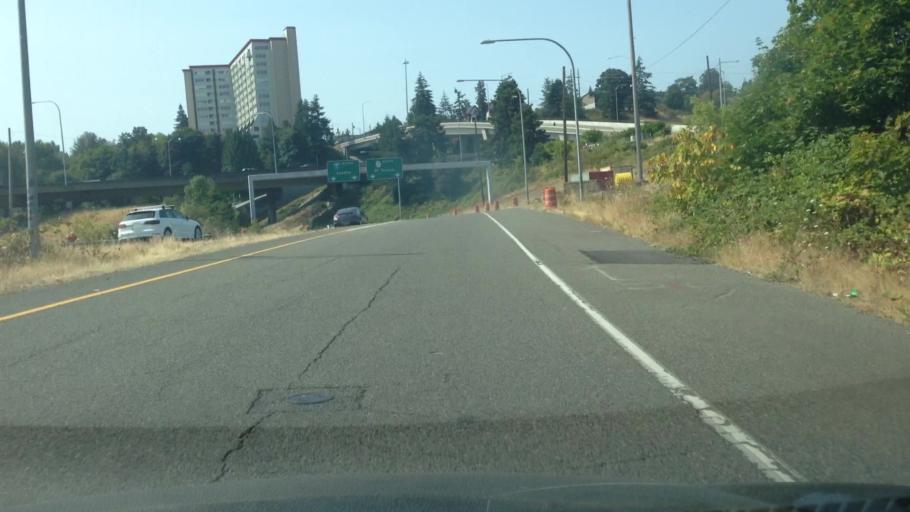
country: US
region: Washington
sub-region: Pierce County
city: Tacoma
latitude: 47.2355
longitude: -122.4328
